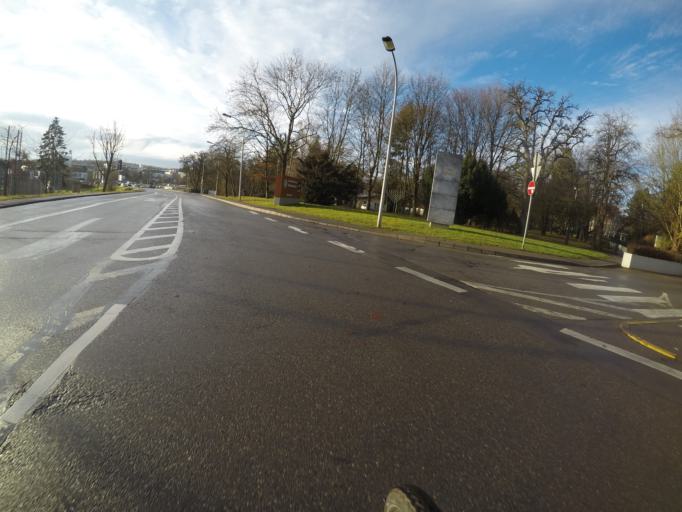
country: DE
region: Baden-Wuerttemberg
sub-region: Regierungsbezirk Stuttgart
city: Gerlingen
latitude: 48.7350
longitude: 9.0878
